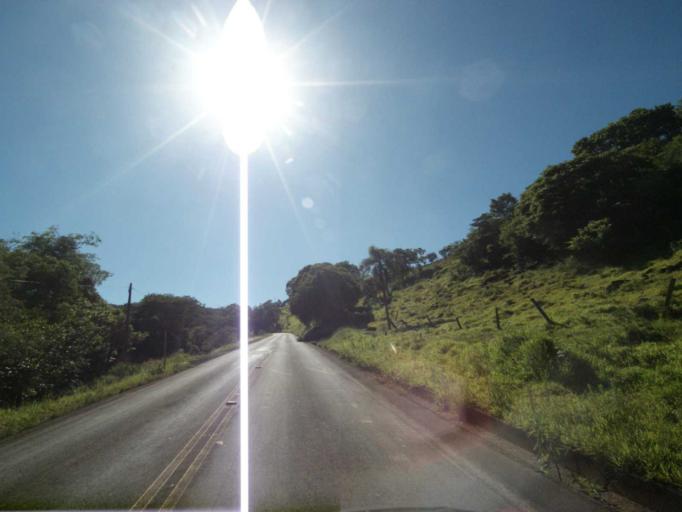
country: BR
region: Parana
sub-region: Francisco Beltrao
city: Francisco Beltrao
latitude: -26.1431
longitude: -53.3017
